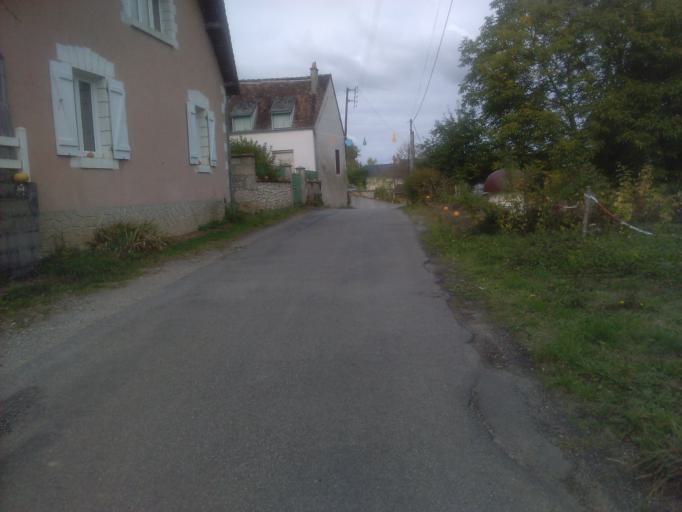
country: FR
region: Centre
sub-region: Departement du Loir-et-Cher
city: Villiers-sur-Loir
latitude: 47.8008
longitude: 0.9793
